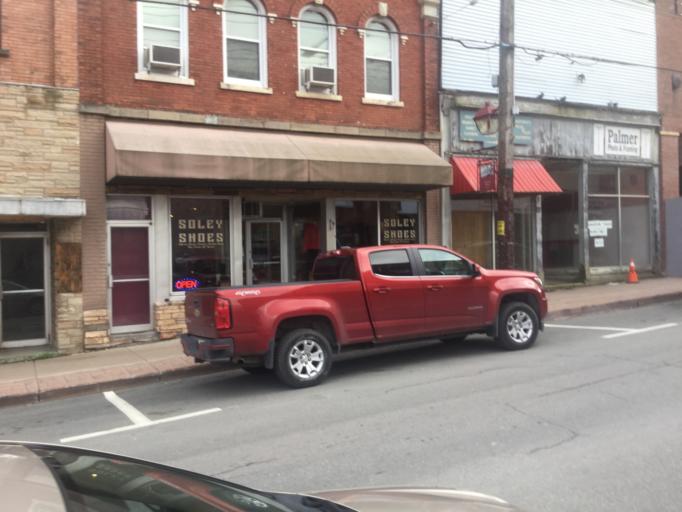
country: CA
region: Nova Scotia
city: New Glasgow
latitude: 45.5869
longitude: -62.6453
